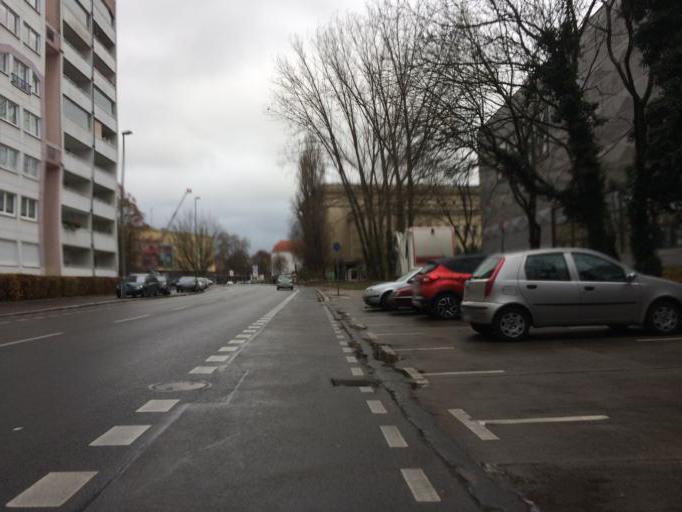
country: DE
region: Berlin
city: Friedrichshain Bezirk
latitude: 52.5126
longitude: 13.4419
